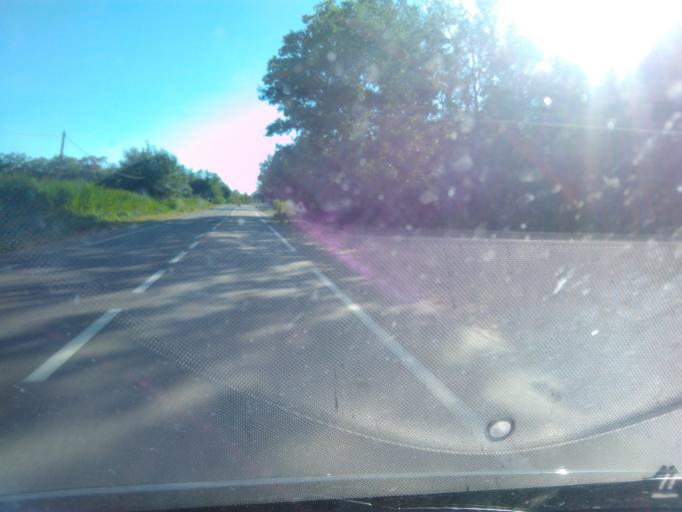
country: FR
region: Languedoc-Roussillon
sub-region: Departement du Gard
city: Saint-Gilles
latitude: 43.6715
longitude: 4.4790
